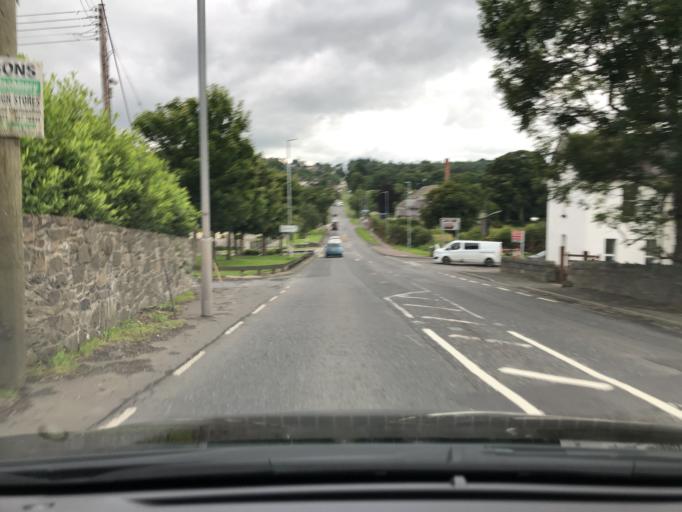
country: GB
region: Northern Ireland
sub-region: Down District
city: Castlewellan
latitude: 54.2649
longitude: -5.9184
